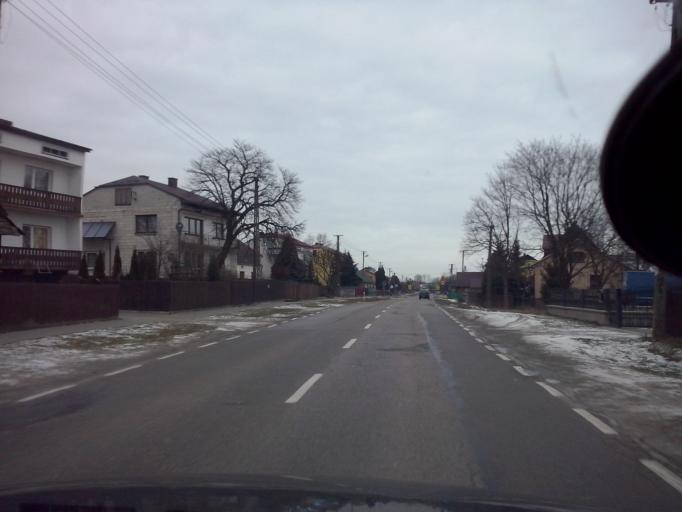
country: PL
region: Lublin Voivodeship
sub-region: Powiat bilgorajski
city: Bilgoraj
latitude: 50.5026
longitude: 22.6449
